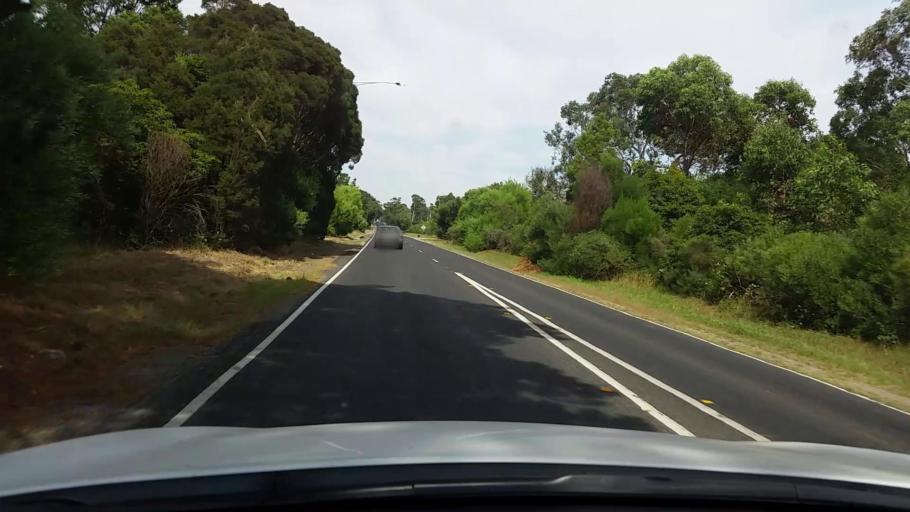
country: AU
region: Victoria
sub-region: Mornington Peninsula
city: Balnarring
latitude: -38.3546
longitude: 145.1537
